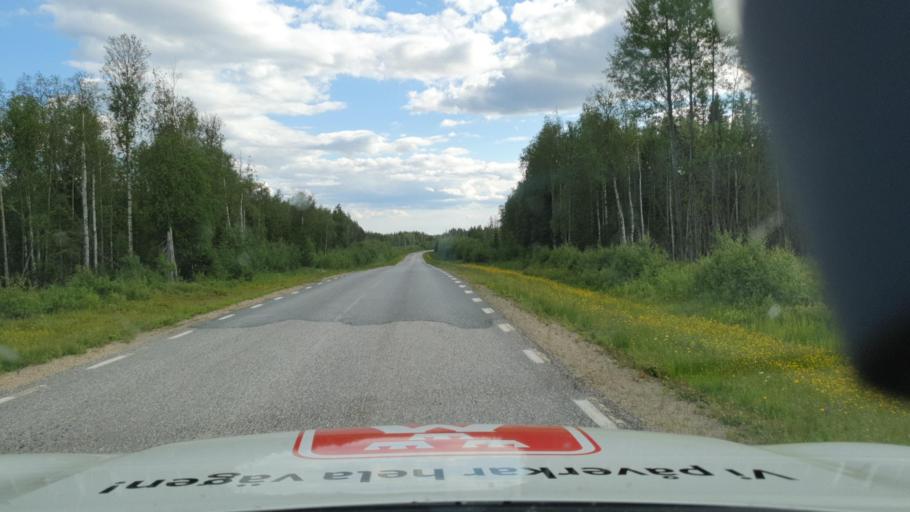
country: SE
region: Vaesterbotten
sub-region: Skelleftea Kommun
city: Langsele
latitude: 64.6620
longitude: 20.0154
